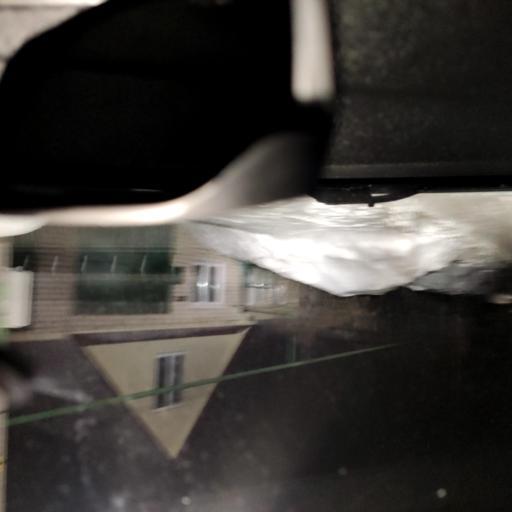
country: RU
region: Tatarstan
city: Stolbishchi
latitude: 55.6991
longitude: 49.1470
